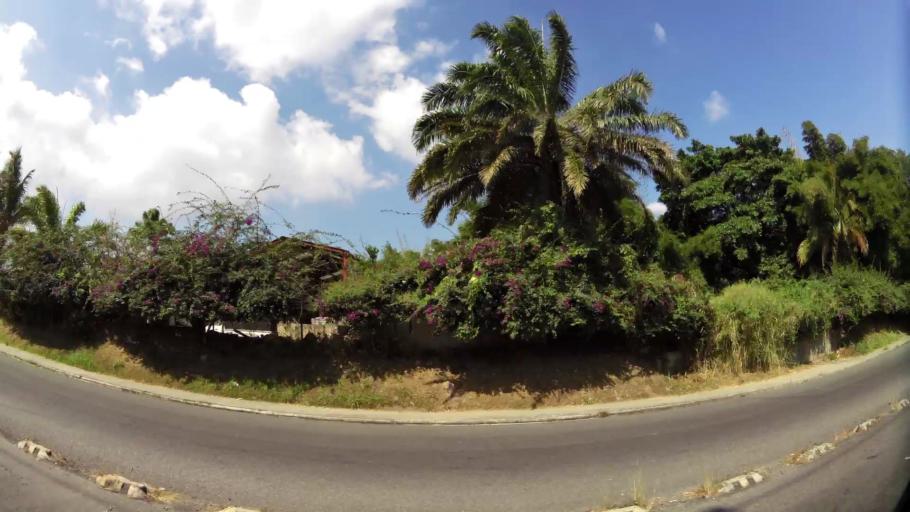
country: SV
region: La Libertad
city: Antiguo Cuscatlan
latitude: 13.6697
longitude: -89.2635
